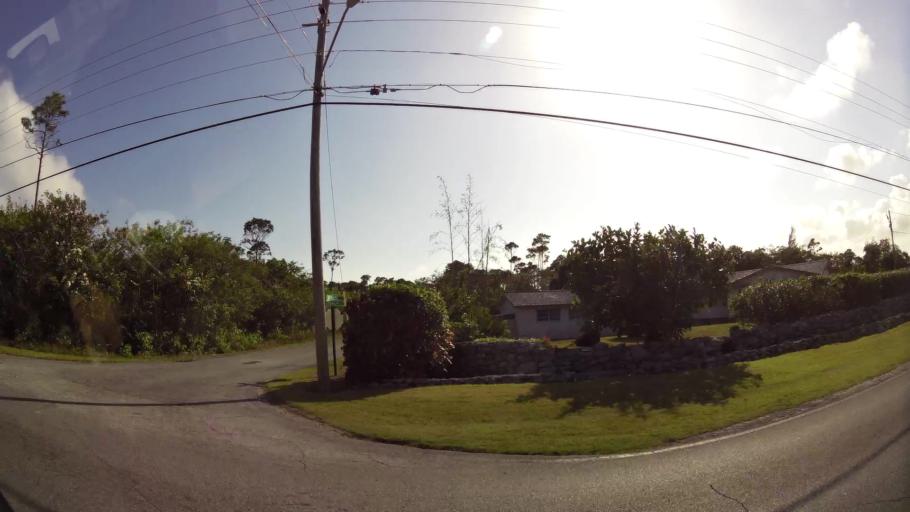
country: BS
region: Freeport
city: Lucaya
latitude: 26.5142
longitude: -78.6642
